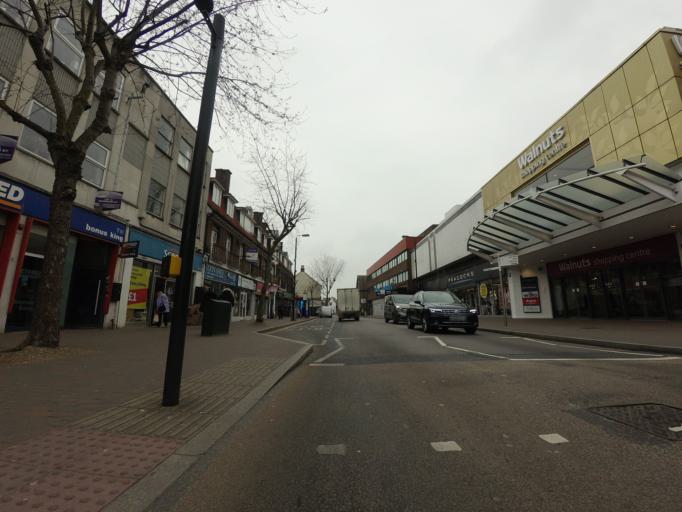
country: GB
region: England
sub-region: Greater London
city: Orpington
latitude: 51.3780
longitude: 0.1010
